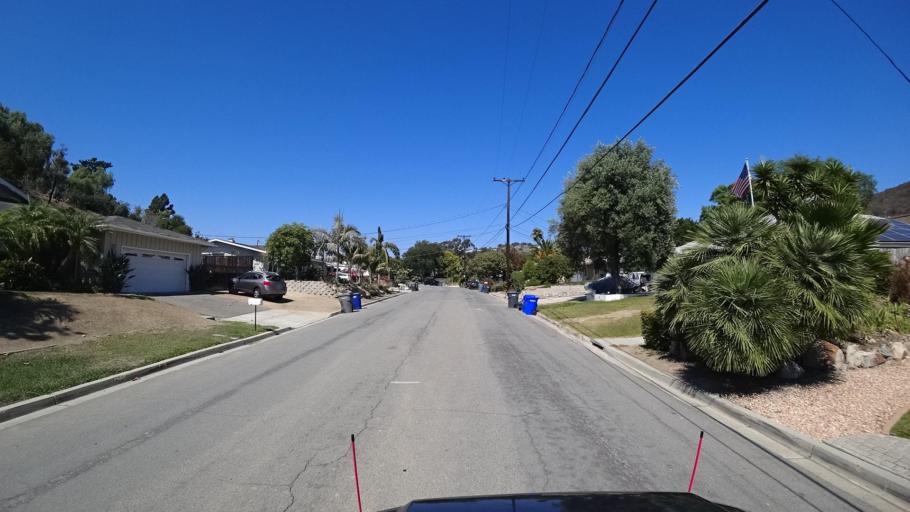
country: US
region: California
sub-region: San Diego County
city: Lake San Marcos
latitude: 33.1152
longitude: -117.2276
